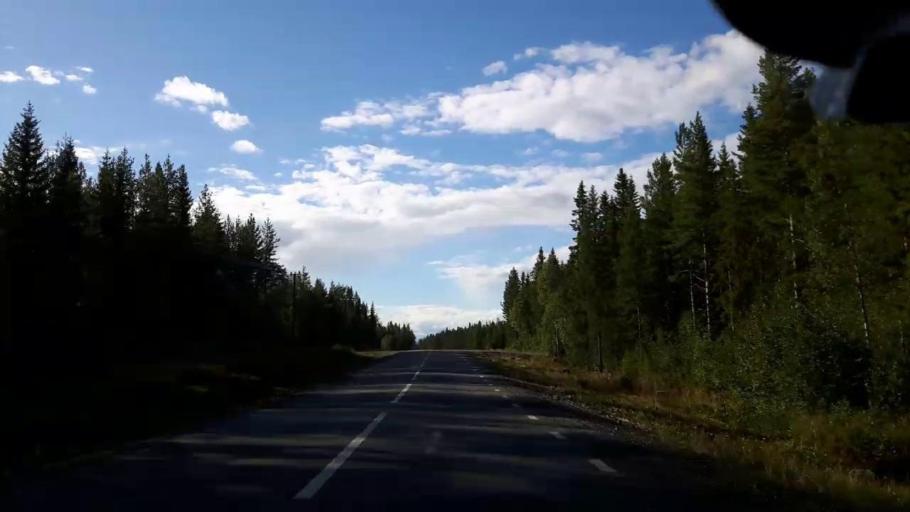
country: SE
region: Jaemtland
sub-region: Stroemsunds Kommun
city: Stroemsund
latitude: 63.5461
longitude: 15.9055
